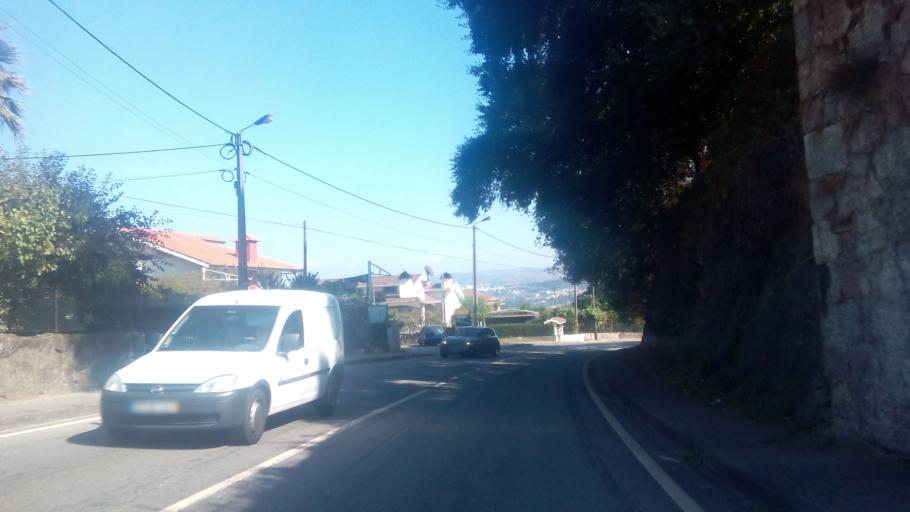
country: PT
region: Porto
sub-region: Paredes
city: Baltar
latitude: 41.1995
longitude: -8.3586
